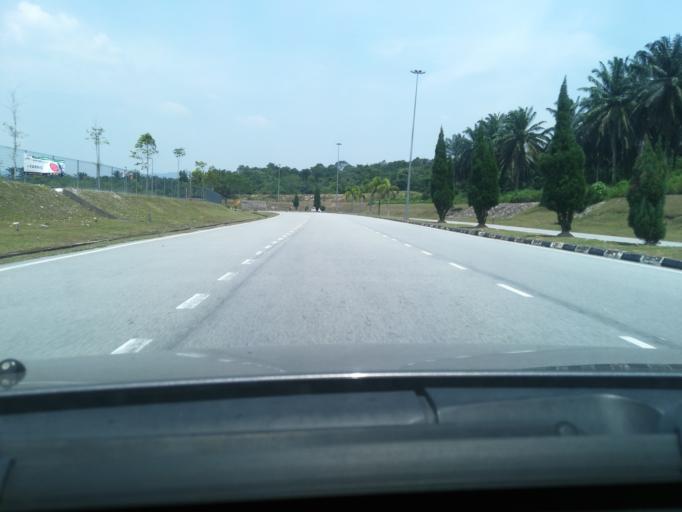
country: MY
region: Kedah
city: Kulim
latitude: 5.4229
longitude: 100.5770
